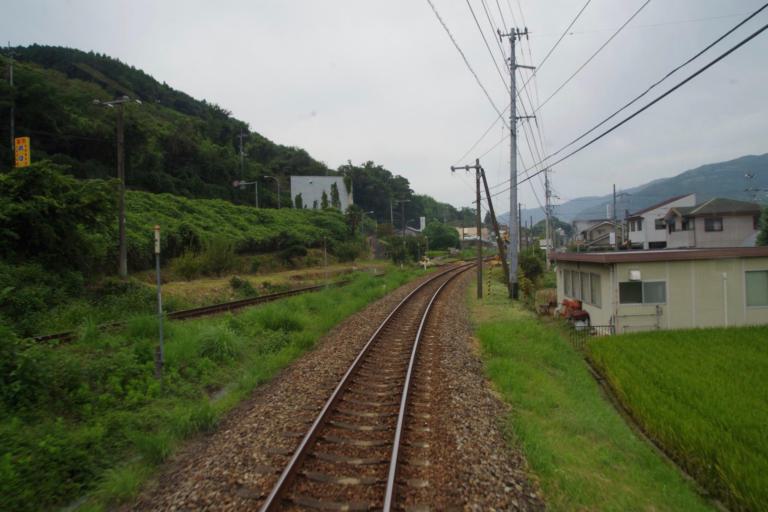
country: JP
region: Tokushima
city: Ikedacho
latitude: 34.0325
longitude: 133.8605
